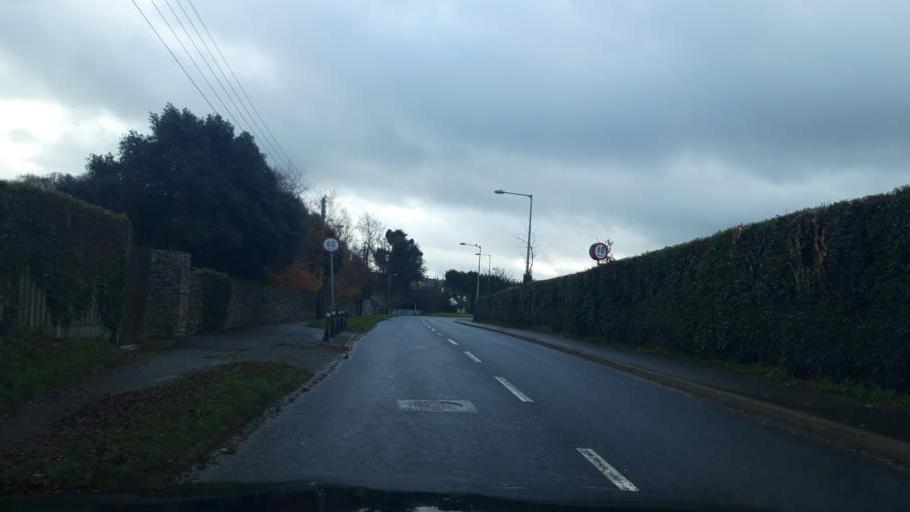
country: IE
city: Newtownmountkennedy
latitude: 53.0875
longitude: -6.1077
